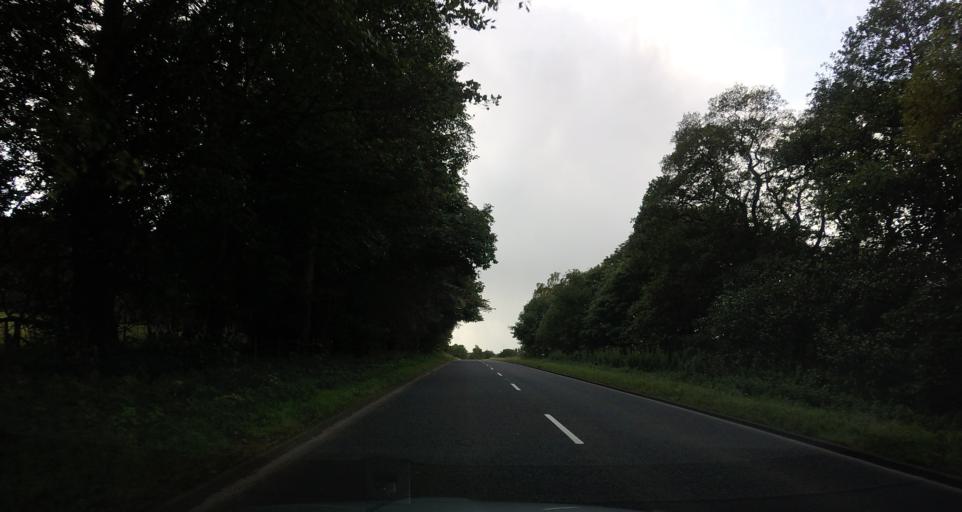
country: GB
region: Scotland
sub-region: Fife
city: Saline
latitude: 56.1788
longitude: -3.5750
